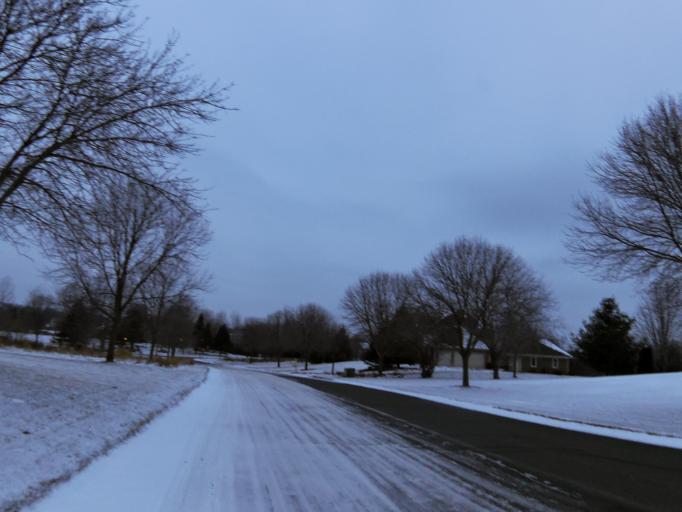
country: US
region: Minnesota
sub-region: Washington County
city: Lakeland
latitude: 44.9586
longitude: -92.8196
